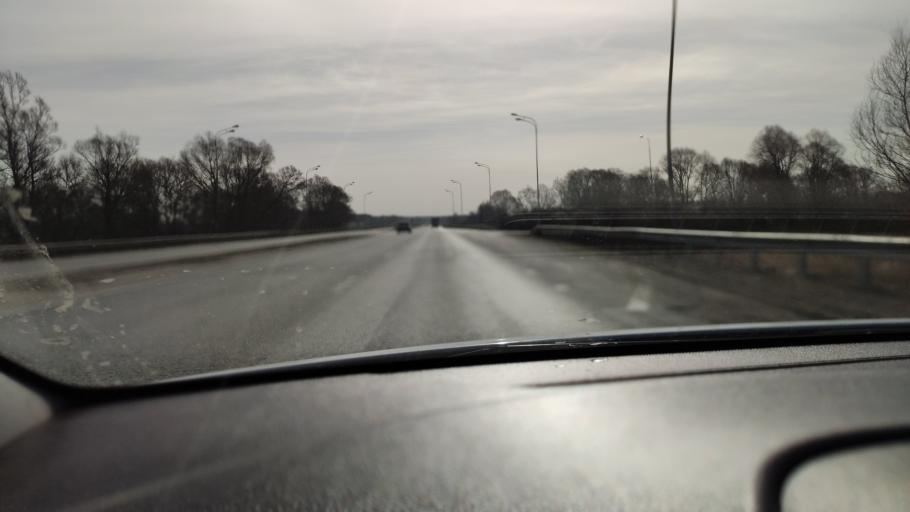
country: RU
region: Tatarstan
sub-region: Gorod Kazan'
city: Kazan
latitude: 55.9098
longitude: 49.1693
